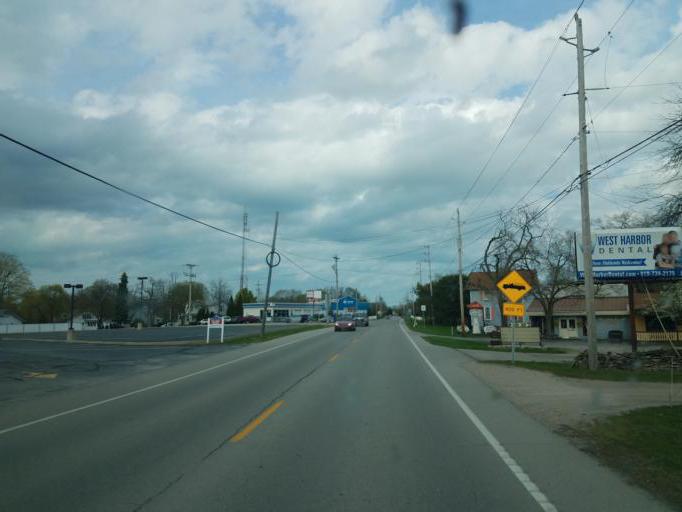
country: US
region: Ohio
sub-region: Erie County
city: Sandusky
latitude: 41.5366
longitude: -82.7526
